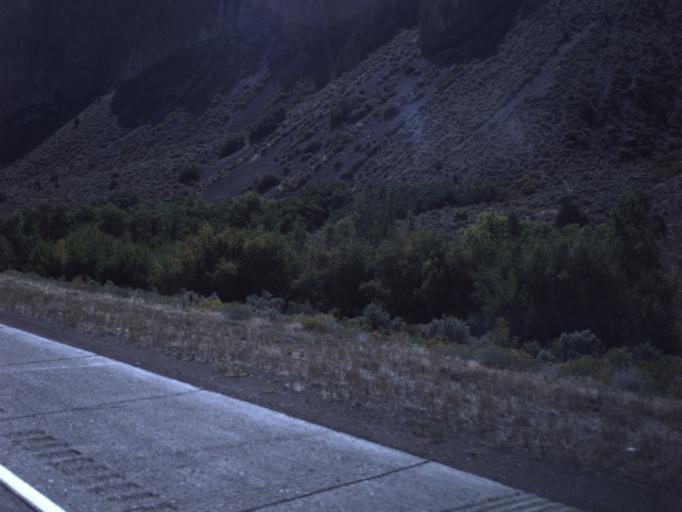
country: US
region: Utah
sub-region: Sevier County
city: Monroe
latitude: 38.5793
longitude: -112.2996
